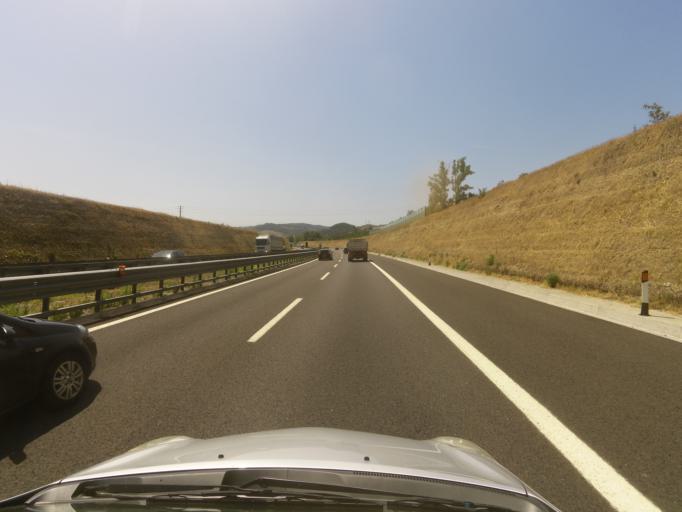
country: IT
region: Emilia-Romagna
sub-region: Provincia di Bologna
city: Grizzana
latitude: 44.2705
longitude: 11.1896
